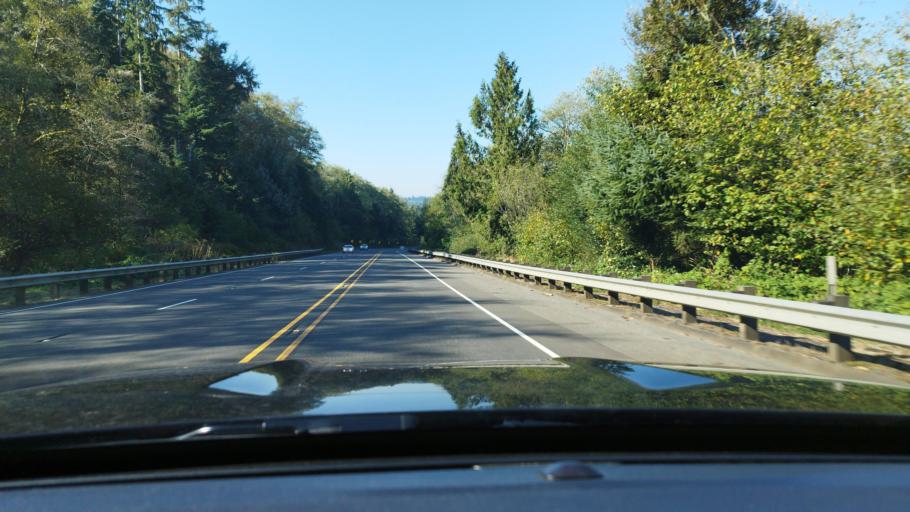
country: US
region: Washington
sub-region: Wahkiakum County
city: Cathlamet
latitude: 46.1701
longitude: -123.5624
